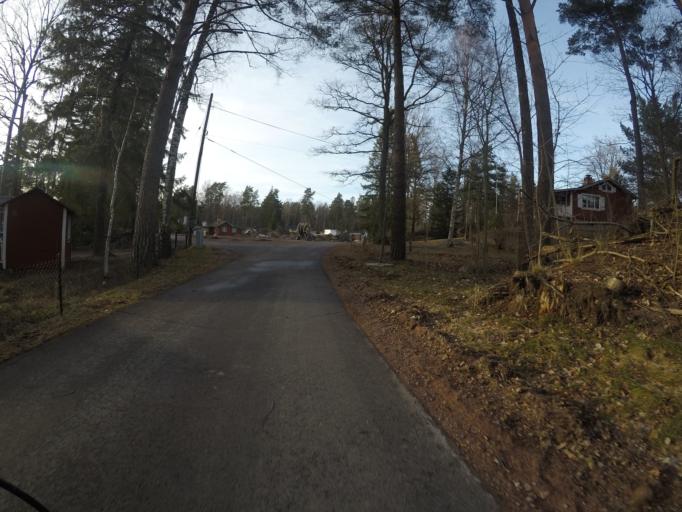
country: SE
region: Soedermanland
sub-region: Eskilstuna Kommun
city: Kvicksund
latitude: 59.4594
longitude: 16.3066
